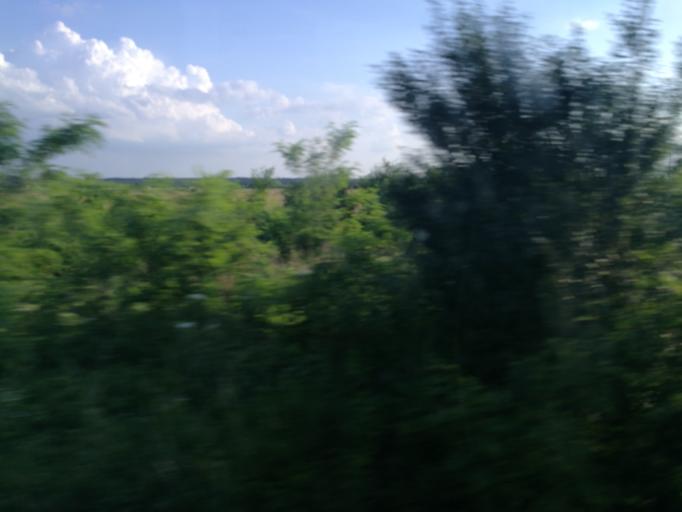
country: RO
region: Arges
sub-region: Comuna Calinesti
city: Vranesti
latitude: 44.8278
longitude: 25.0033
